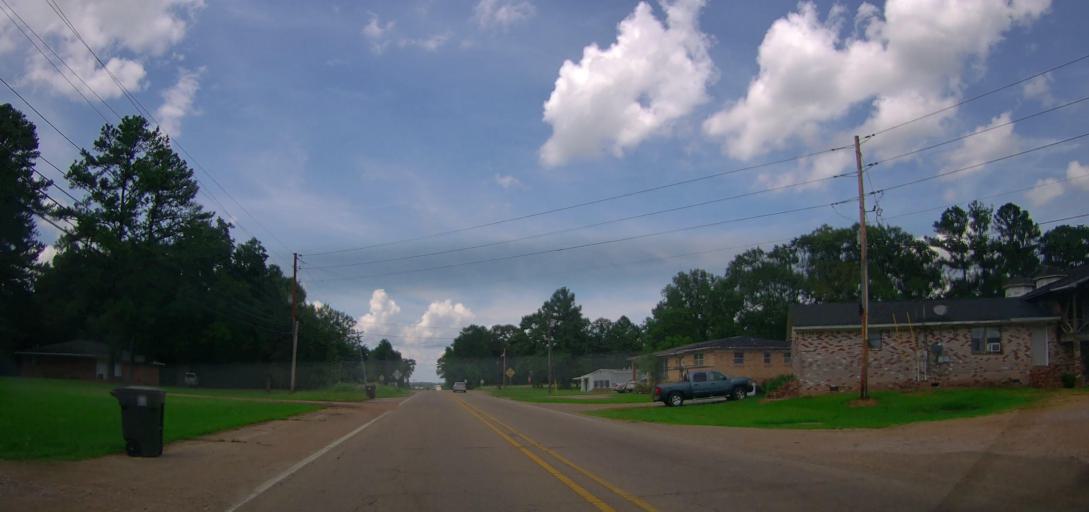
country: US
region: Mississippi
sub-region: Lee County
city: Shannon
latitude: 34.1296
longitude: -88.7193
